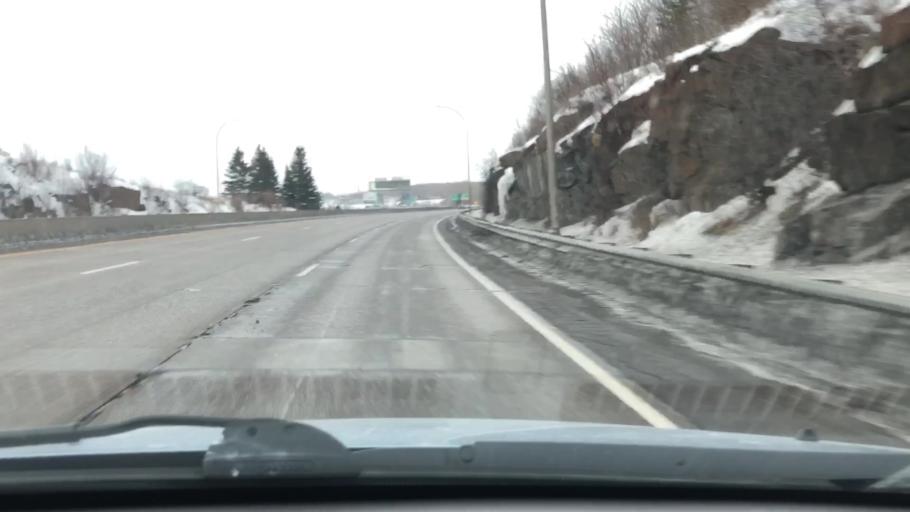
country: US
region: Minnesota
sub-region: Saint Louis County
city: Proctor
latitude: 46.7371
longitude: -92.1887
